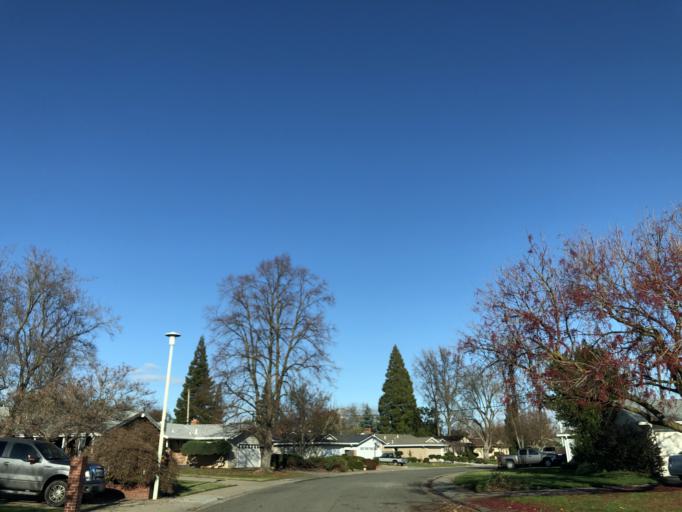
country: US
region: California
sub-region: Sacramento County
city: Rosemont
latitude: 38.5535
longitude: -121.4023
